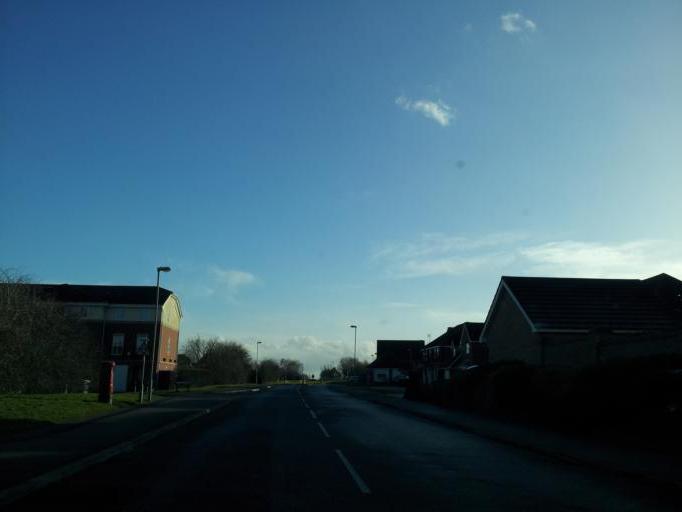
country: GB
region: England
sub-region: Nottinghamshire
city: Newark on Trent
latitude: 53.0745
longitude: -0.7722
